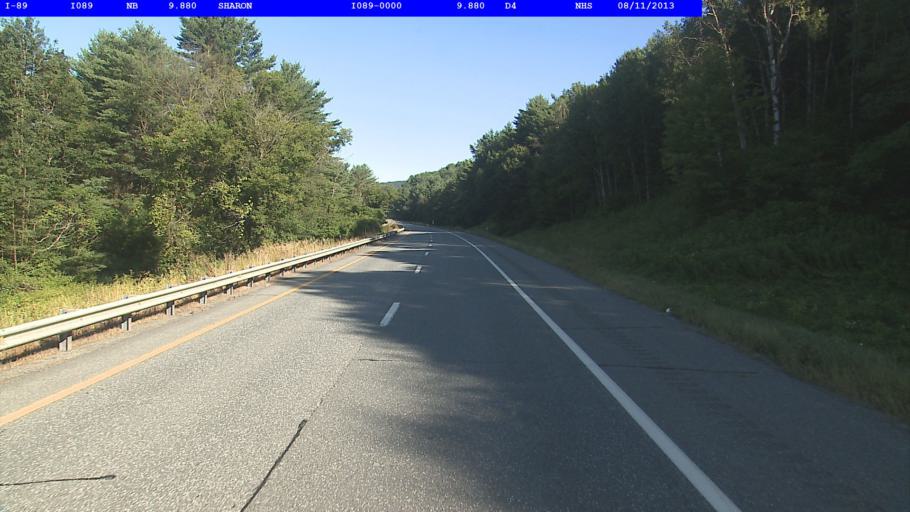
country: US
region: Vermont
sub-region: Windsor County
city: Wilder
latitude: 43.7401
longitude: -72.4346
